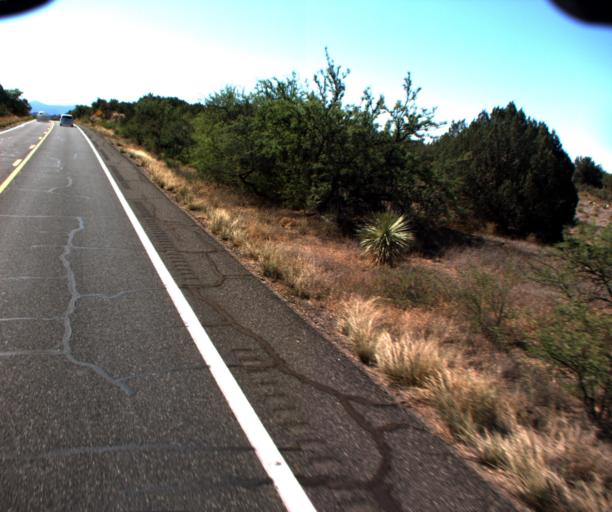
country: US
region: Arizona
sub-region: Yavapai County
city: Lake Montezuma
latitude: 34.7039
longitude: -111.7697
